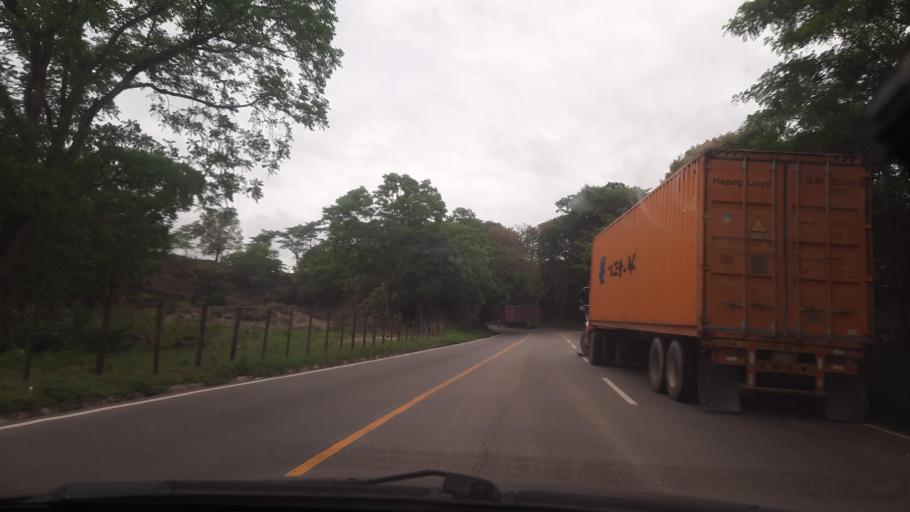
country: GT
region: Izabal
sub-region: Municipio de Los Amates
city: Los Amates
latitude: 15.2534
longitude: -89.1128
